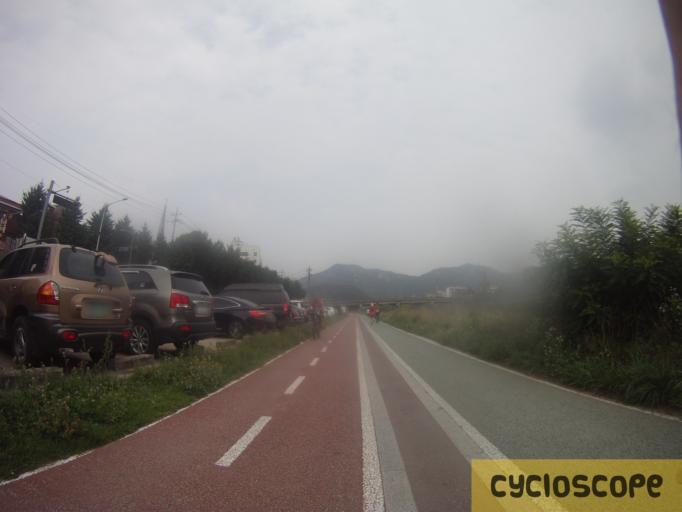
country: KR
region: Gyeonggi-do
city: Anyang-si
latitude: 37.4091
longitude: 126.9117
